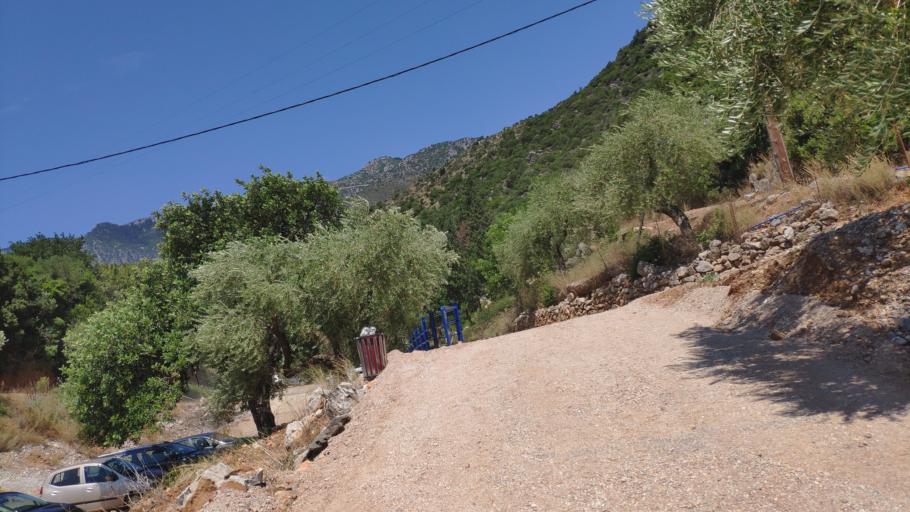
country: GR
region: Peloponnese
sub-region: Nomos Lakonias
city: Sykea
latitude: 36.9846
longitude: 22.9972
